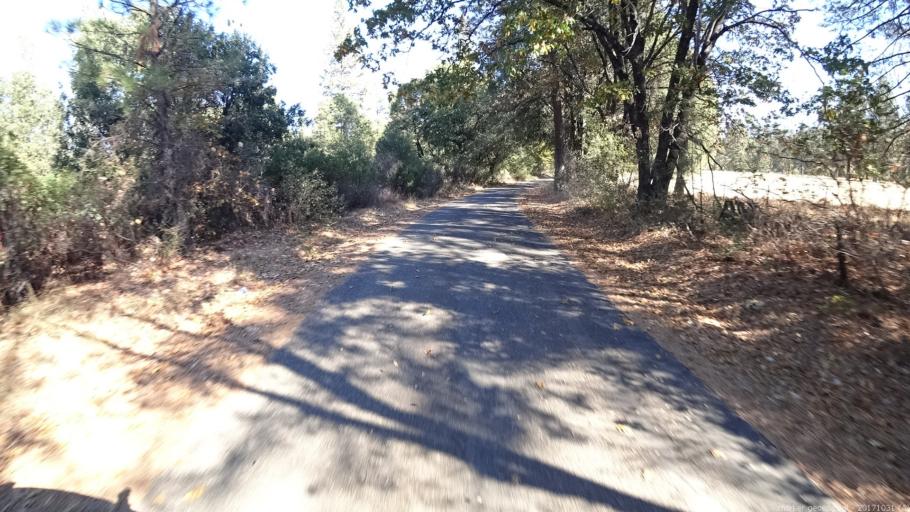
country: US
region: California
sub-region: Shasta County
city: Shingletown
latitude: 40.5327
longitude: -121.9392
